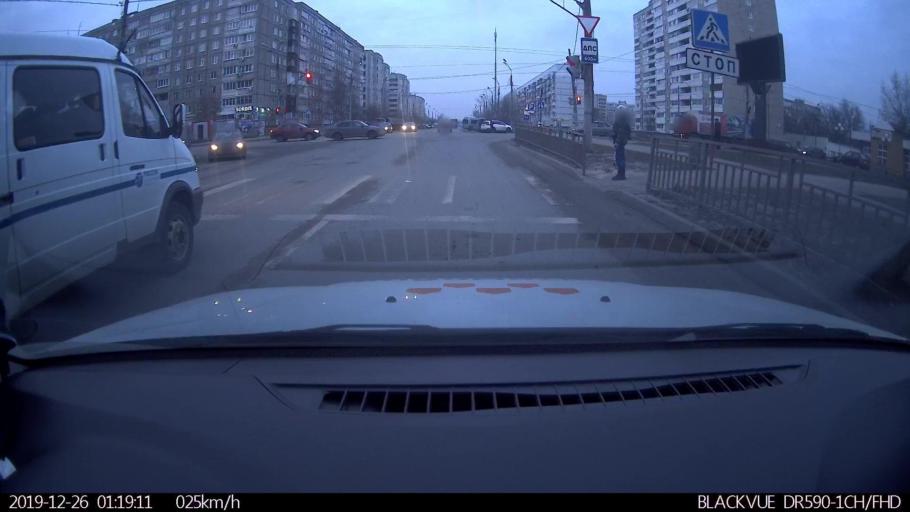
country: RU
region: Nizjnij Novgorod
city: Nizhniy Novgorod
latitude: 56.2705
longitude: 43.8886
